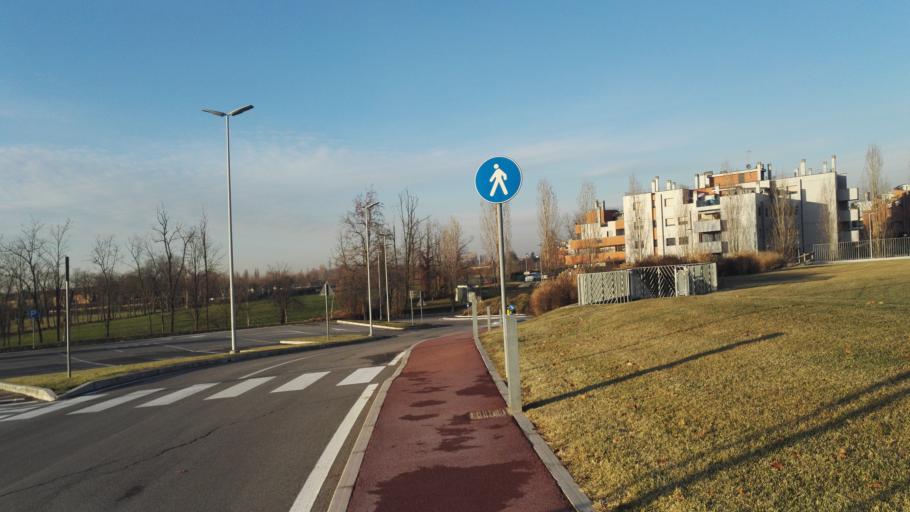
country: IT
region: Lombardy
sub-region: Citta metropolitana di Milano
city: San Bovio-San Felice
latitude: 45.4602
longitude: 9.3071
